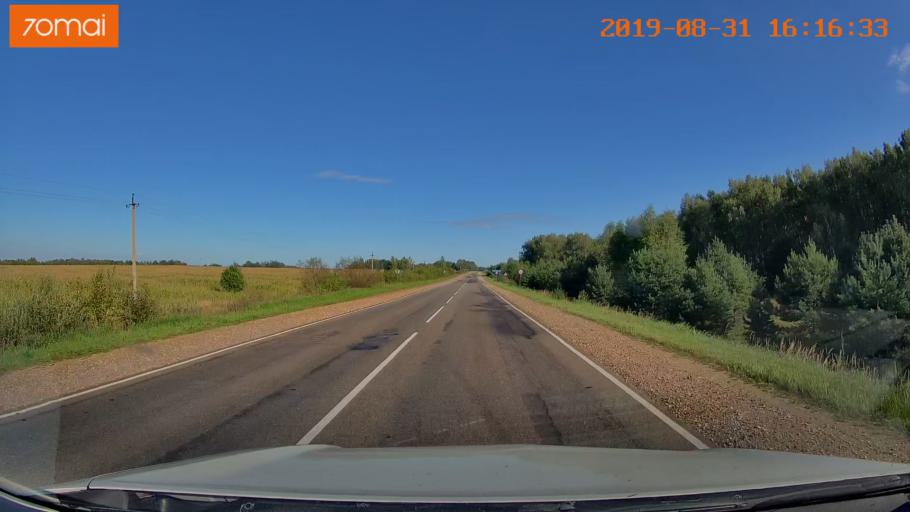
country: RU
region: Kaluga
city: Nikola-Lenivets
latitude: 54.5524
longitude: 35.5132
